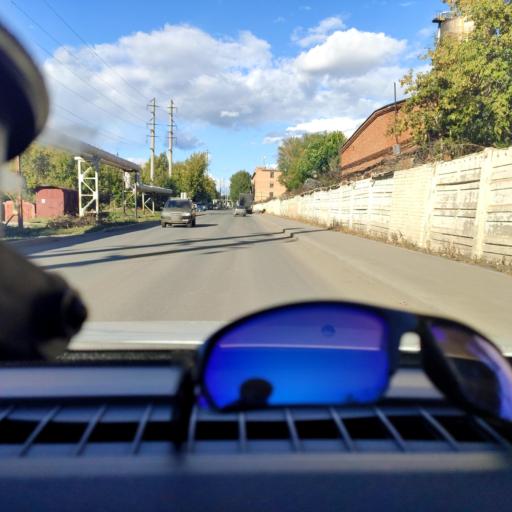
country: RU
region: Samara
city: Chapayevsk
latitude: 52.9744
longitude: 49.7143
